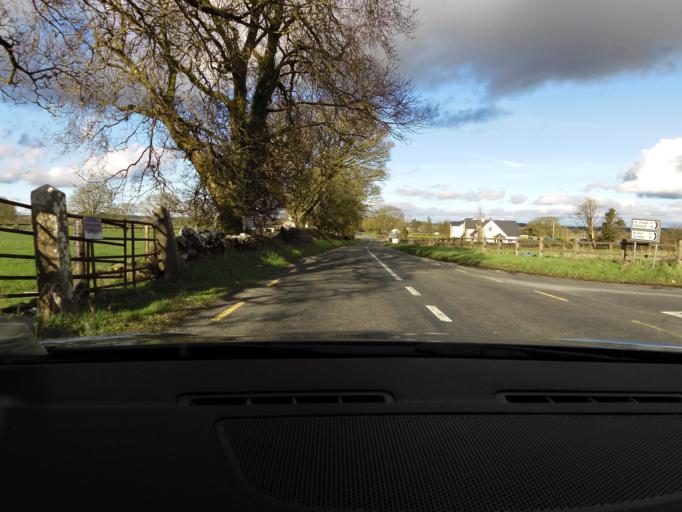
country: IE
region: Connaught
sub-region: Roscommon
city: Castlerea
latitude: 53.6889
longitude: -8.4738
